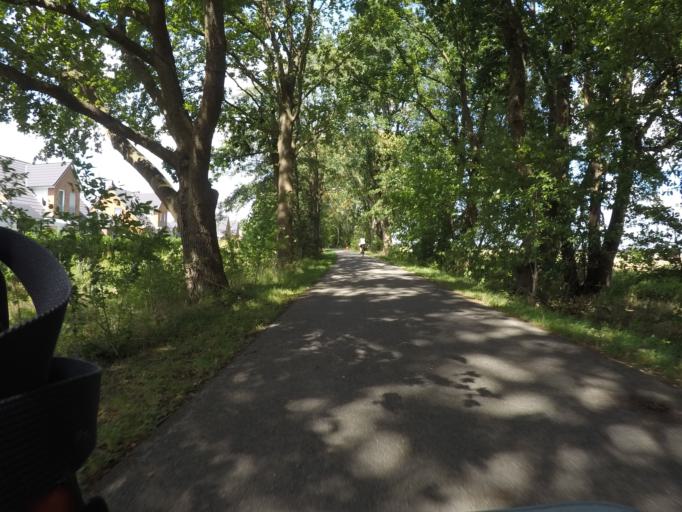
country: DE
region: Lower Saxony
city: Stelle
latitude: 53.4482
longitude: 10.1292
